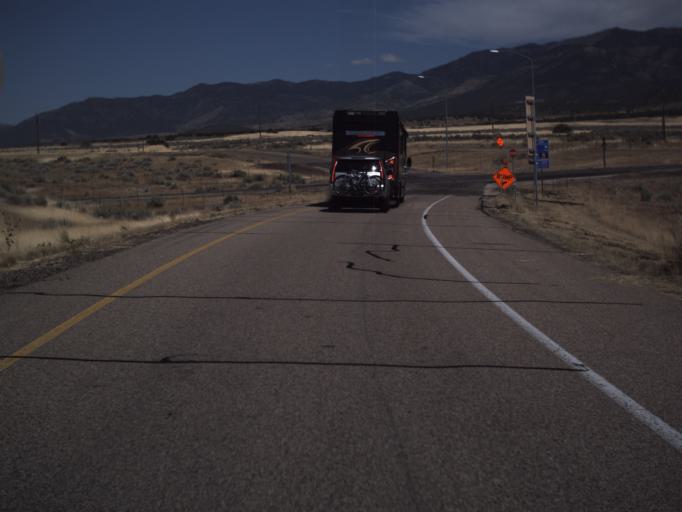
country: US
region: Utah
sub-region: Millard County
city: Fillmore
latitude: 38.9906
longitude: -112.3247
